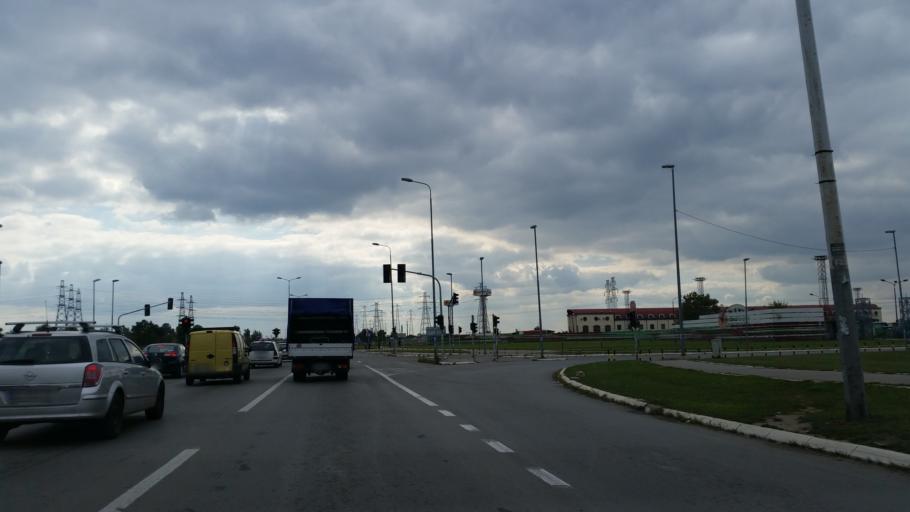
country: RS
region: Central Serbia
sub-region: Belgrade
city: Zemun
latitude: 44.8272
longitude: 20.3622
